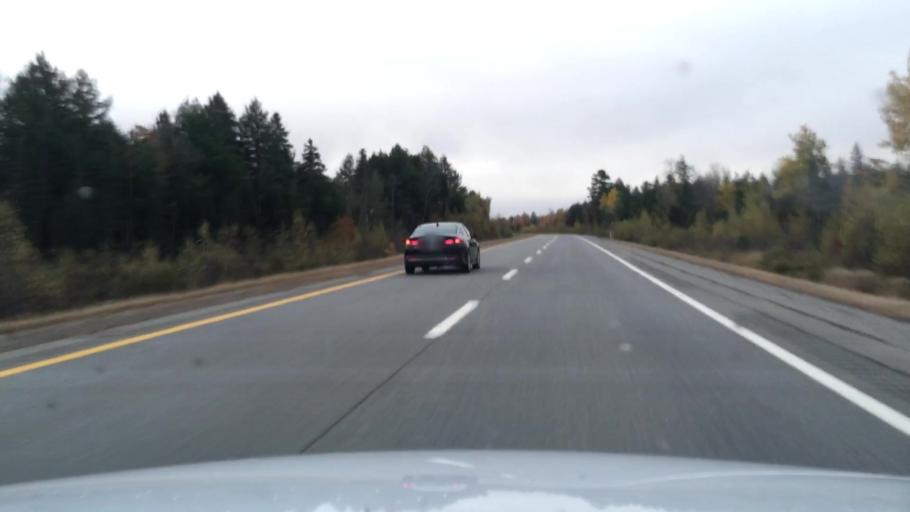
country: US
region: Maine
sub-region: Penobscot County
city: Greenbush
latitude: 45.1034
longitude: -68.6960
